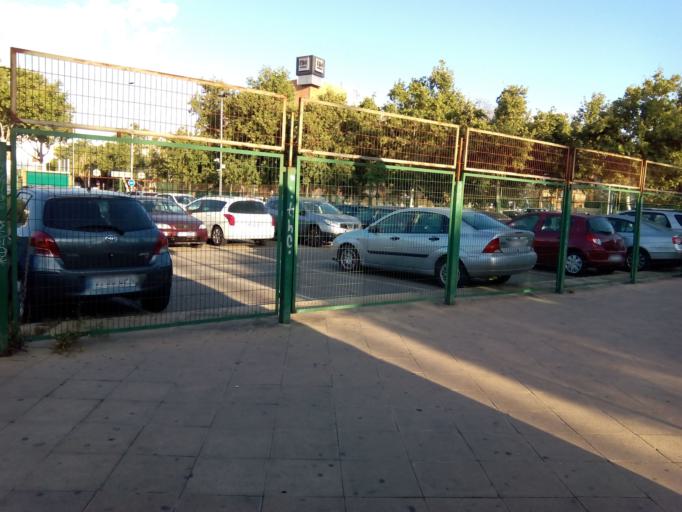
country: ES
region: Andalusia
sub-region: Provincia de Sevilla
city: Camas
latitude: 37.3936
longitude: -6.0035
